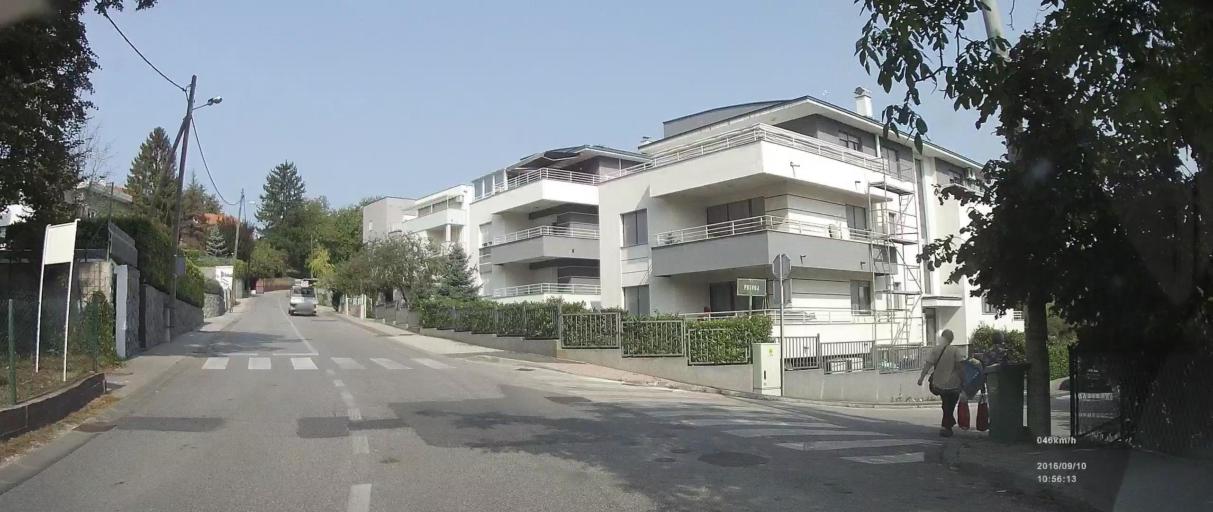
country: HR
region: Grad Zagreb
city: Zagreb
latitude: 45.8352
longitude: 15.9371
